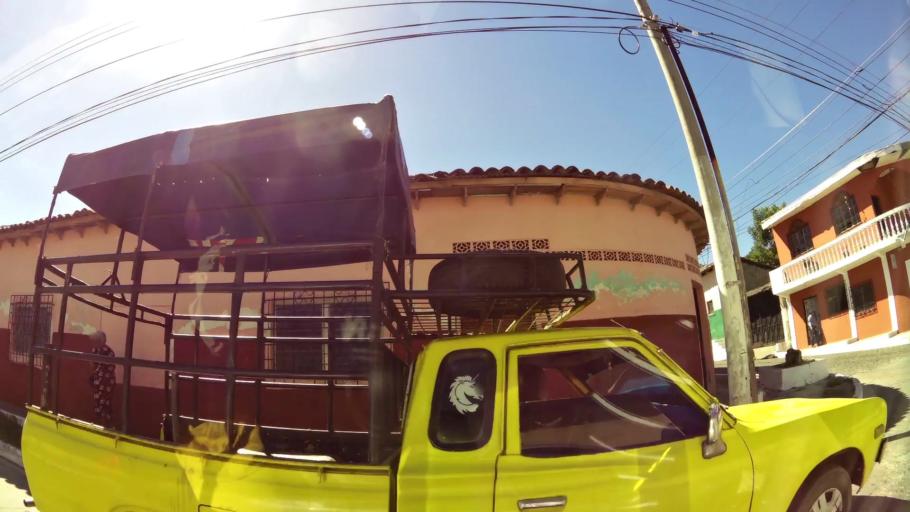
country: SV
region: La Libertad
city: San Juan Opico
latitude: 13.8781
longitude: -89.3590
